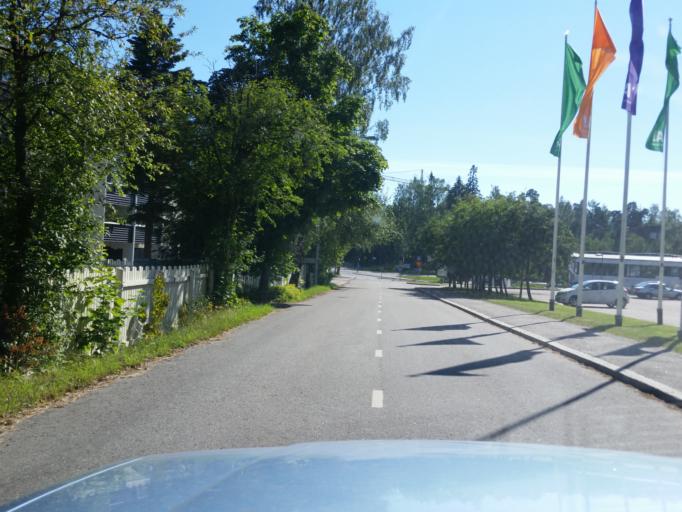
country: FI
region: Uusimaa
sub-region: Helsinki
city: Otaniemi
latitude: 60.1845
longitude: 24.8328
